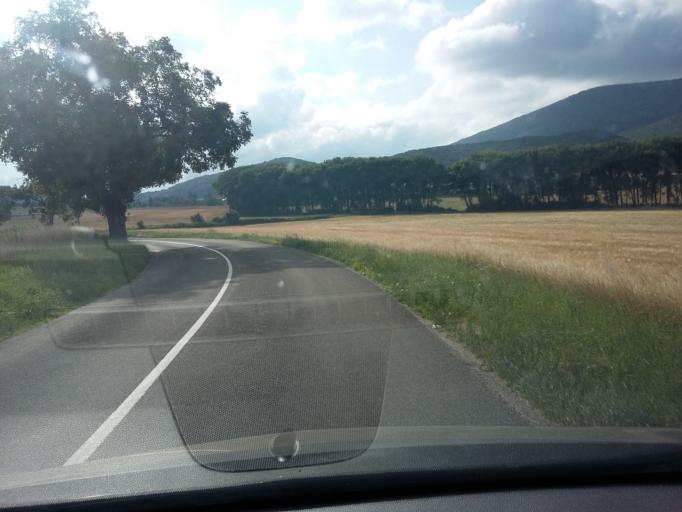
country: SK
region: Trnavsky
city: Smolenice
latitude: 48.5432
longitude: 17.3772
